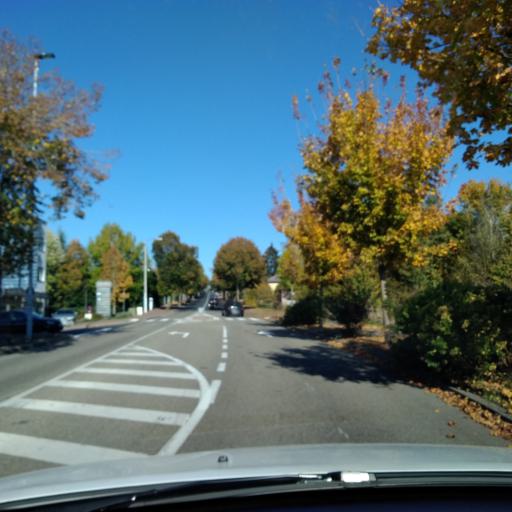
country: FR
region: Lorraine
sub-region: Departement de la Moselle
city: Neufgrange
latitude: 49.0923
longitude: 7.0414
